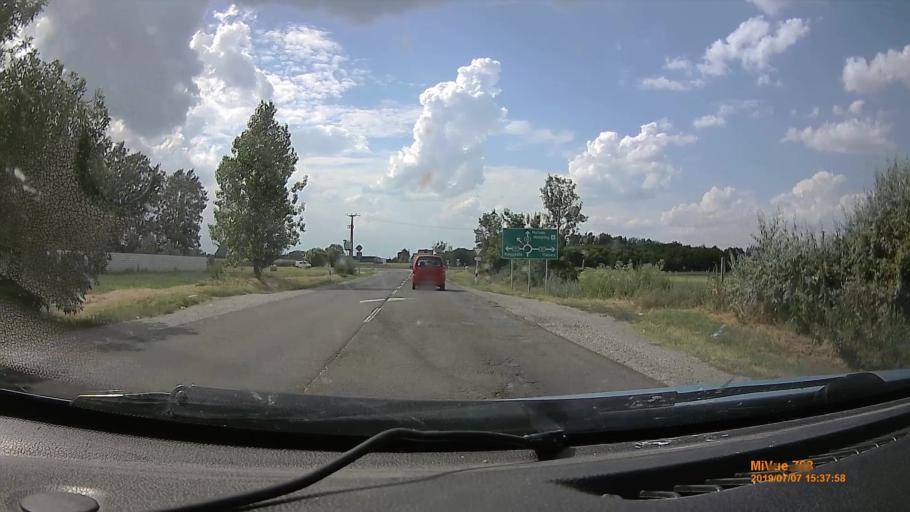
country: HU
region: Jasz-Nagykun-Szolnok
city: Jaszbereny
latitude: 47.4885
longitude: 19.9440
